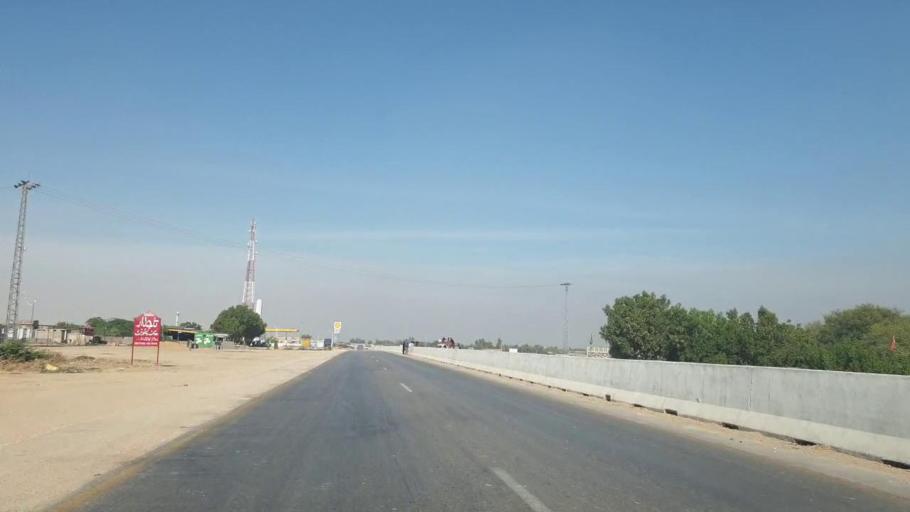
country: PK
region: Sindh
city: Hala
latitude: 25.7026
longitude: 68.2957
